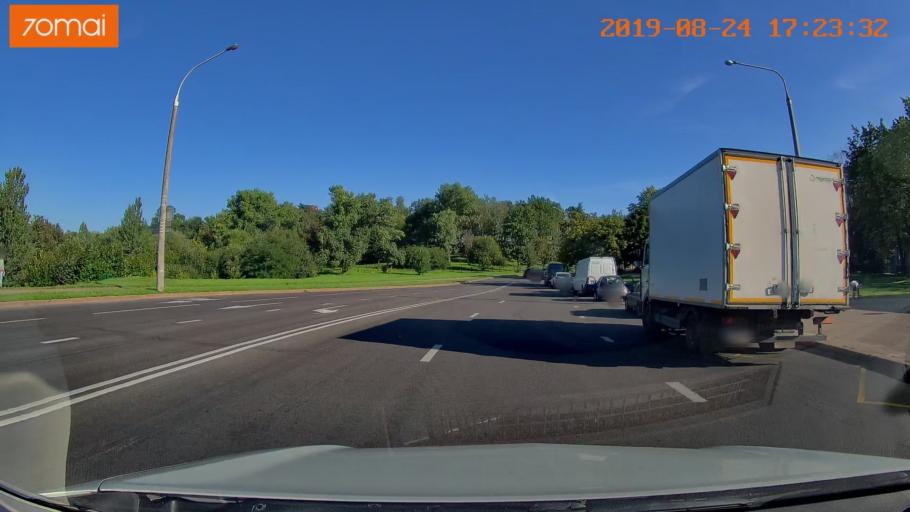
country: BY
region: Minsk
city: Hatava
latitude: 53.8423
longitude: 27.6513
